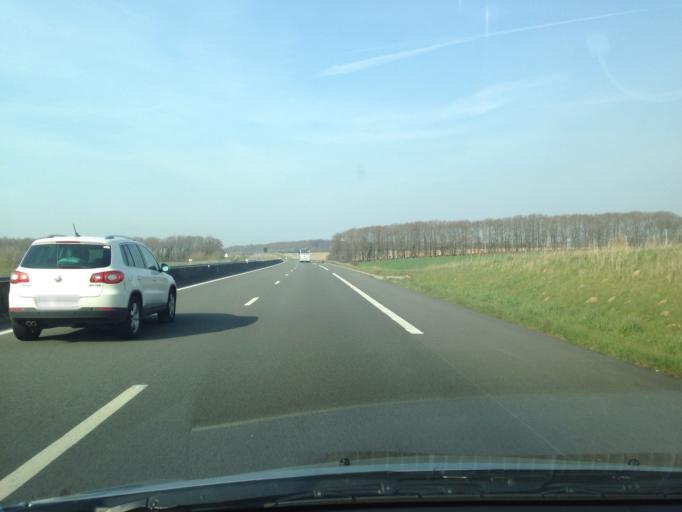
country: FR
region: Nord-Pas-de-Calais
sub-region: Departement du Pas-de-Calais
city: Verton
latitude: 50.3678
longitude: 1.6935
